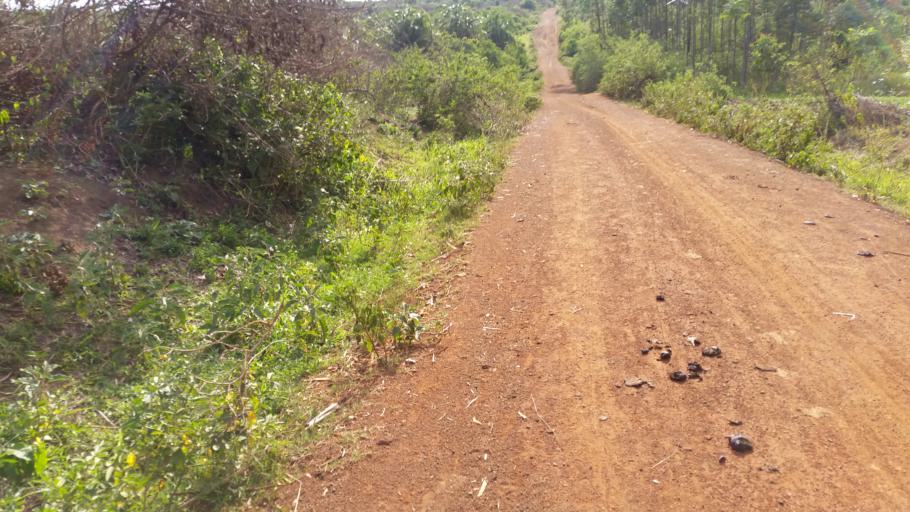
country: UG
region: Eastern Region
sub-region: Busia District
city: Busia
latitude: 0.5501
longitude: 33.9984
